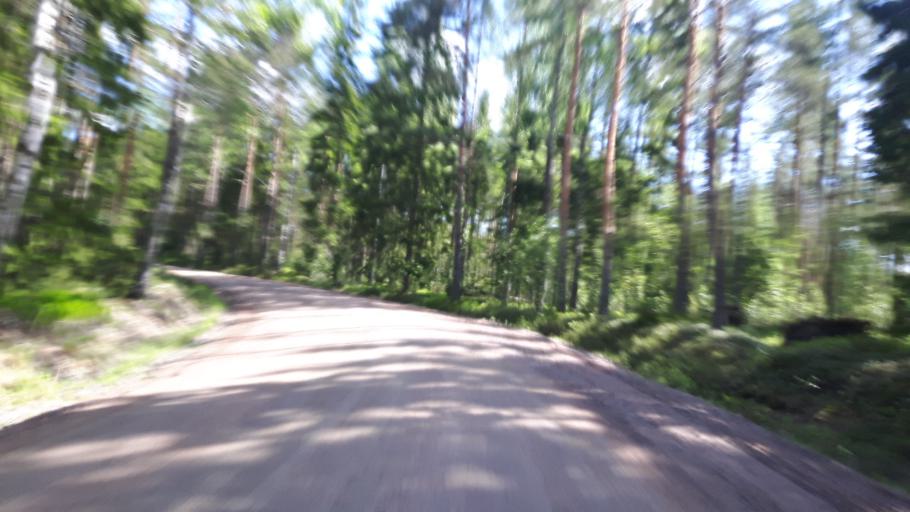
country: FI
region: Kymenlaakso
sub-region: Kotka-Hamina
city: Hamina
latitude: 60.5238
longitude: 27.2782
